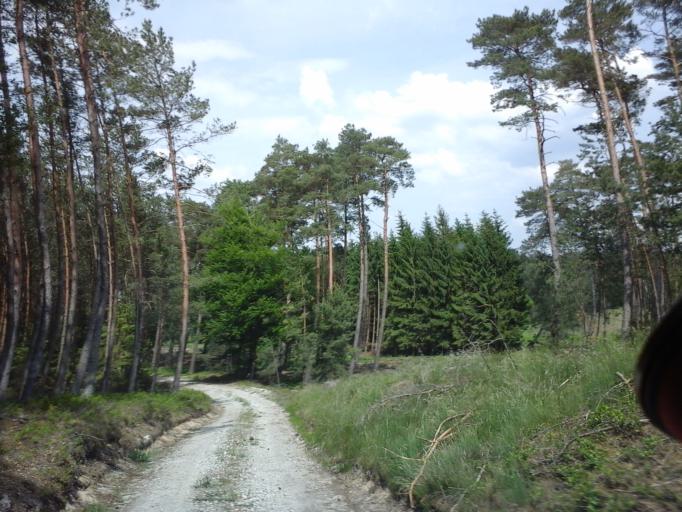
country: PL
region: West Pomeranian Voivodeship
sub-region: Powiat choszczenski
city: Drawno
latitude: 53.1290
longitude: 15.7619
